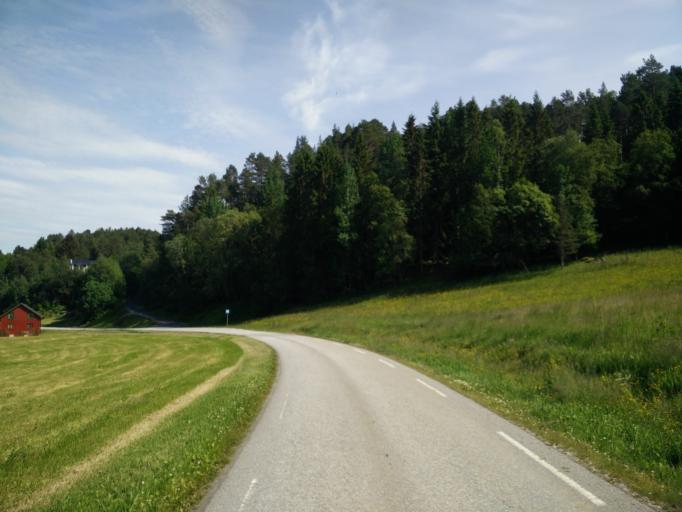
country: NO
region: More og Romsdal
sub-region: Kristiansund
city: Rensvik
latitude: 63.0186
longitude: 7.9502
